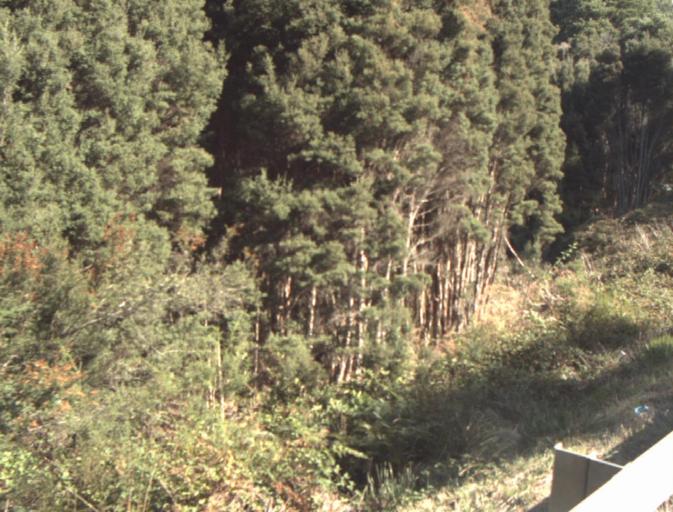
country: AU
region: Tasmania
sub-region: Launceston
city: Mayfield
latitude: -41.3361
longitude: 147.1714
